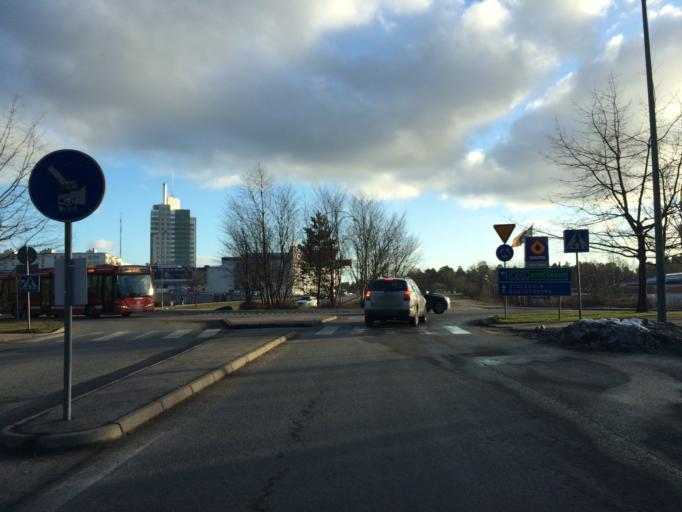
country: SE
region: Stockholm
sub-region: Nacka Kommun
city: Nacka
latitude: 59.3135
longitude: 18.1626
